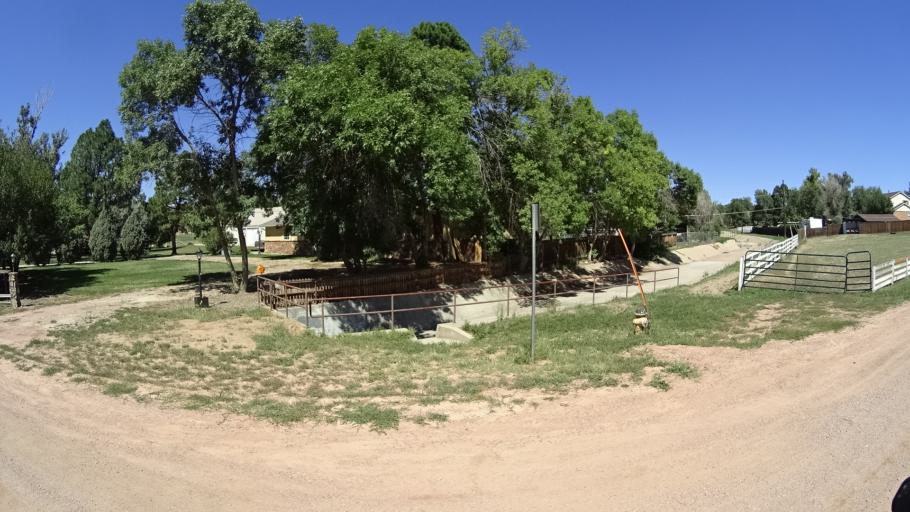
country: US
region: Colorado
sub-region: El Paso County
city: Cimarron Hills
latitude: 38.8631
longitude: -104.7322
